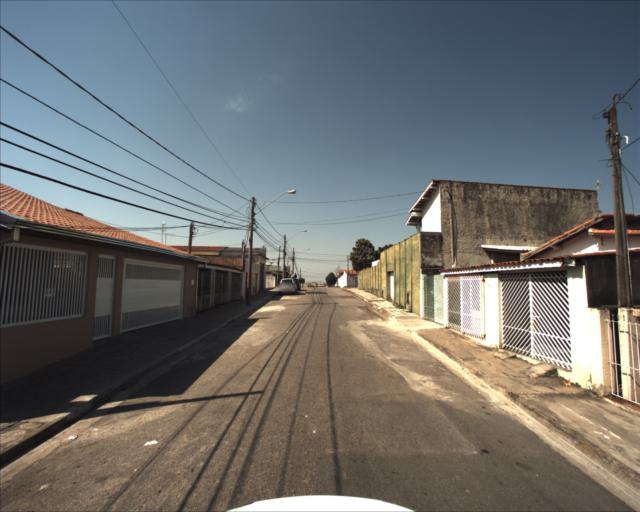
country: BR
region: Sao Paulo
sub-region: Sorocaba
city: Sorocaba
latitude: -23.4810
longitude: -47.4714
